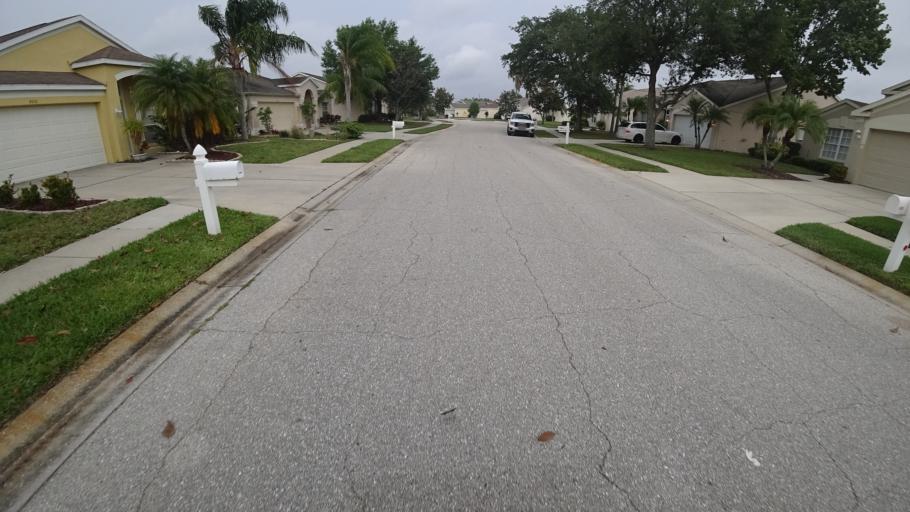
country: US
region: Florida
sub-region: Manatee County
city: Samoset
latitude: 27.4588
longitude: -82.5040
